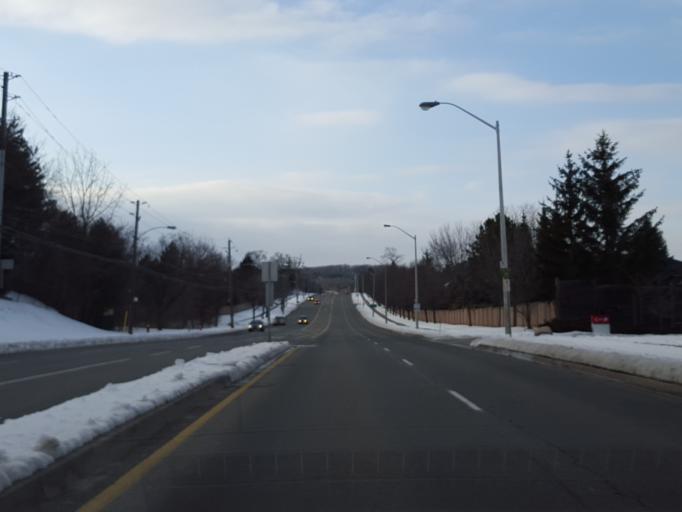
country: CA
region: Ontario
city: Burlington
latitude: 43.3575
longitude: -79.8444
